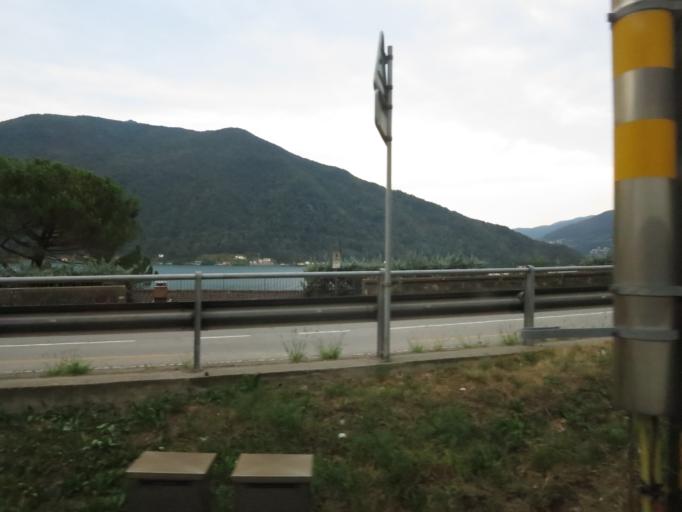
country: CH
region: Ticino
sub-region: Lugano District
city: Melano
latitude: 45.9389
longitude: 8.9681
